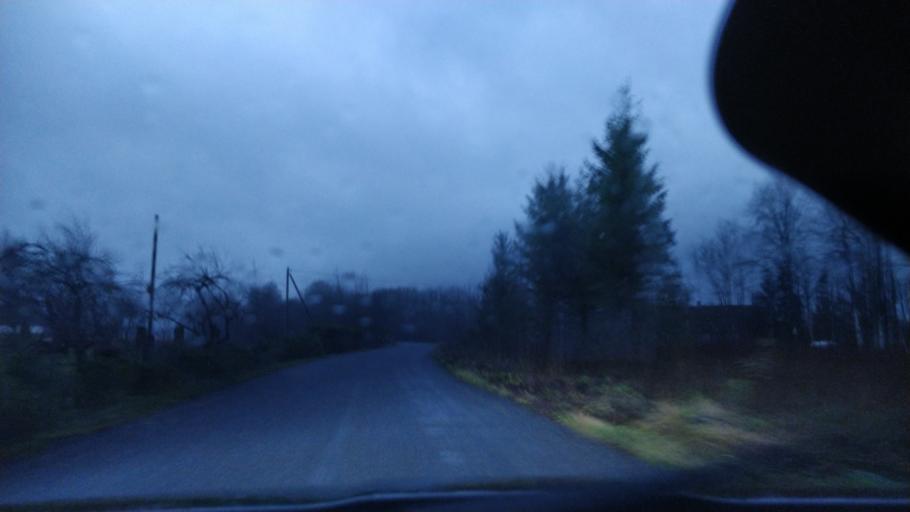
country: EE
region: Laeaene
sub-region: Lihula vald
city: Lihula
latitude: 58.8547
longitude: 24.0109
